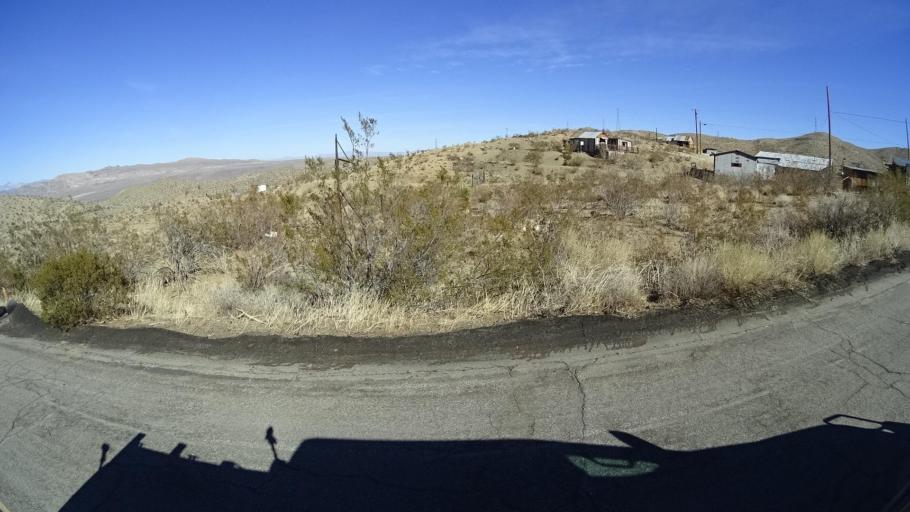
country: US
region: California
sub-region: Kern County
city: Ridgecrest
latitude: 35.3687
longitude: -117.6584
